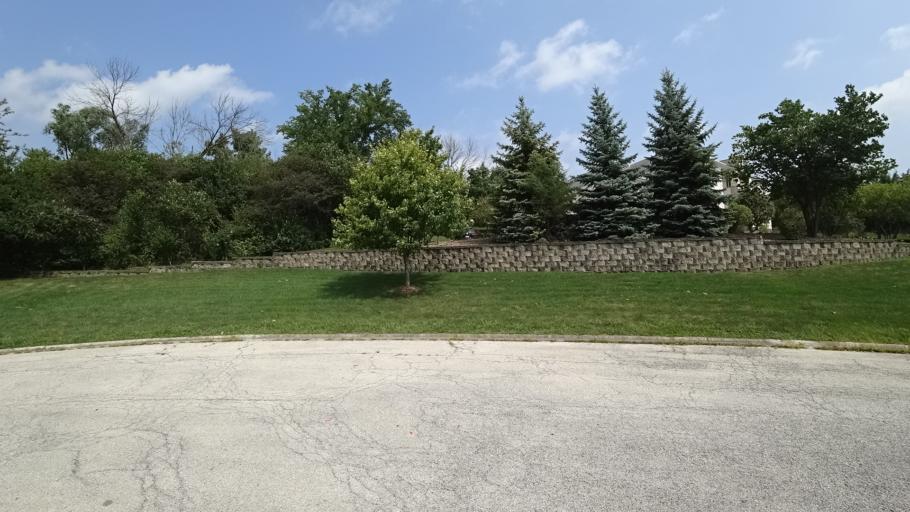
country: US
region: Illinois
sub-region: Cook County
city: Orland Park
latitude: 41.6179
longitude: -87.8856
